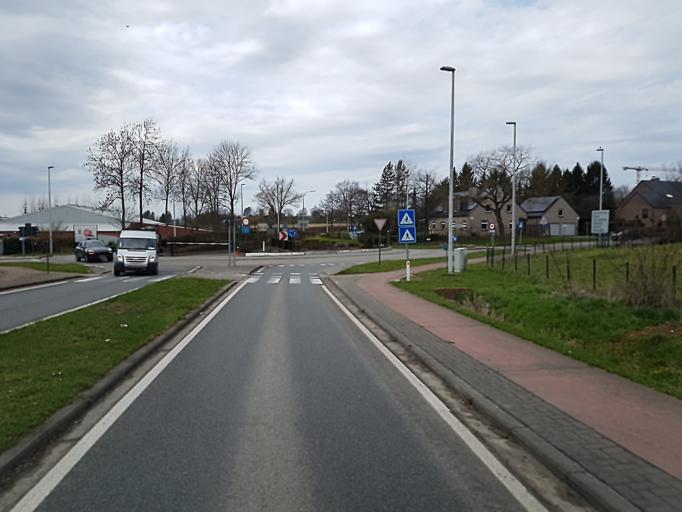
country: BE
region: Flanders
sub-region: Provincie Limburg
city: Borgloon
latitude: 50.7992
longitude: 5.3415
